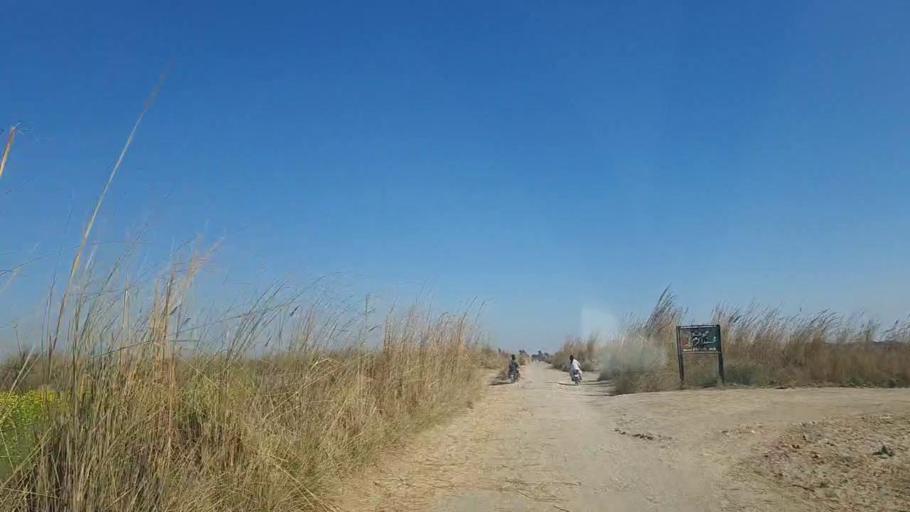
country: PK
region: Sindh
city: Khadro
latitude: 26.2094
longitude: 68.8345
